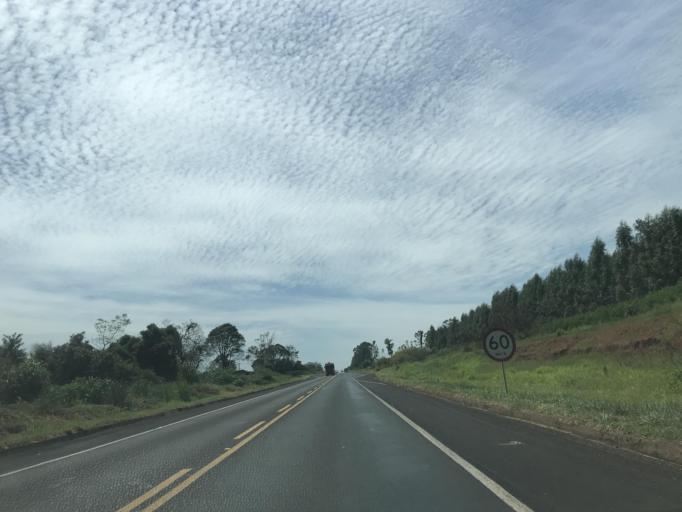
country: BR
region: Parana
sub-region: Paranavai
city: Paranavai
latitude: -22.9999
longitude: -52.5662
